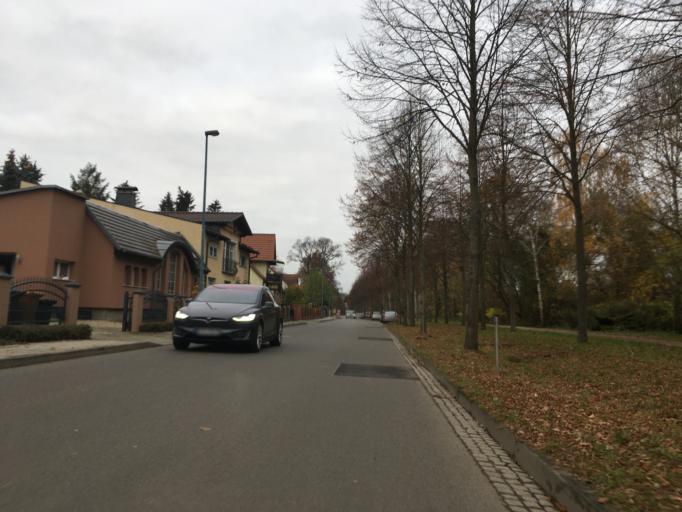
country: DE
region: Brandenburg
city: Frankfurt (Oder)
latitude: 52.3189
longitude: 14.5540
